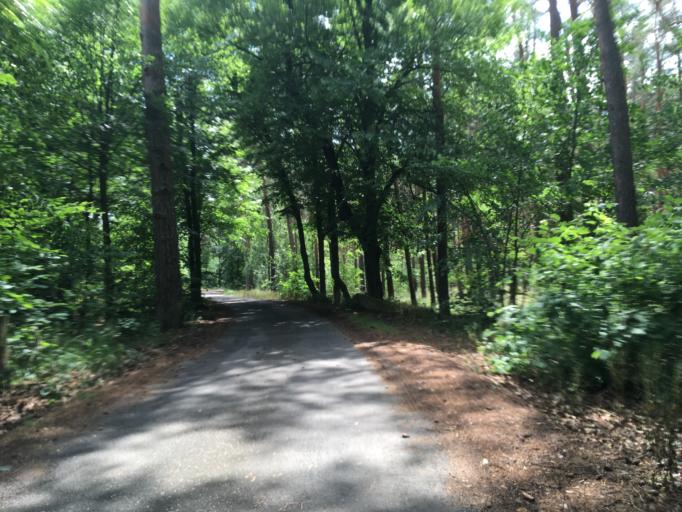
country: DE
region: Berlin
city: Schmockwitz
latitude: 52.3937
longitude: 13.6524
